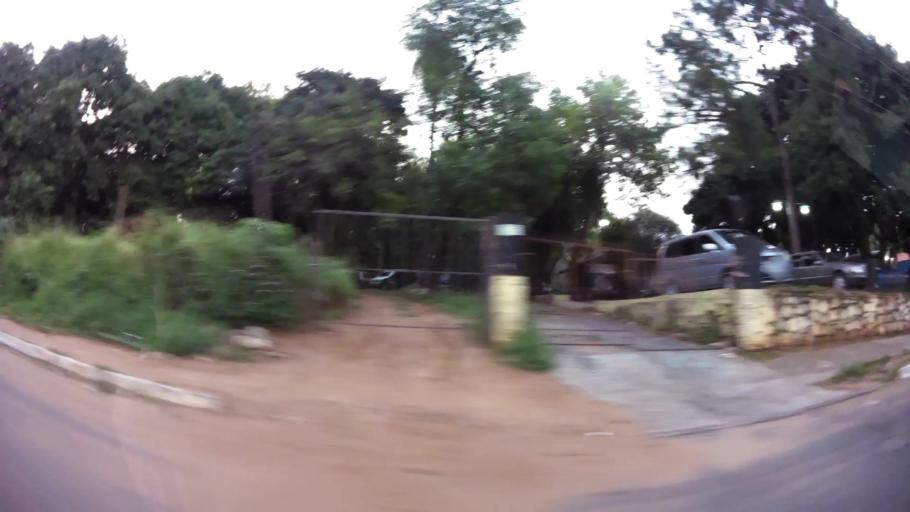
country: PY
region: Asuncion
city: Asuncion
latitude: -25.3189
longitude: -57.6142
